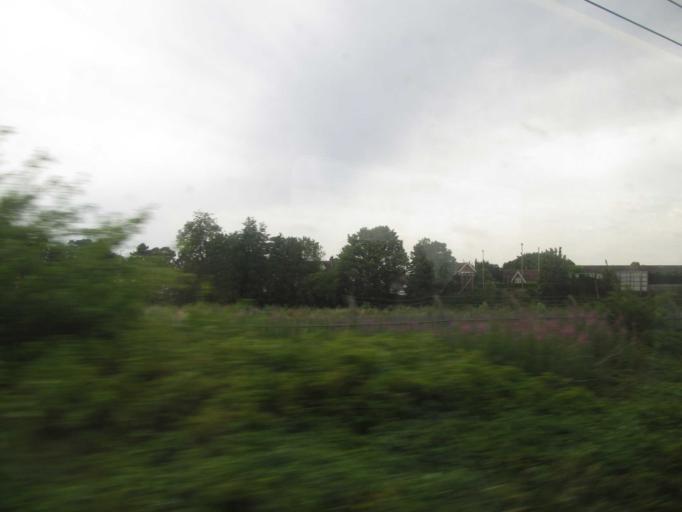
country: GB
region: England
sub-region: Bedford
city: Bedford
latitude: 52.1243
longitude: -0.4779
